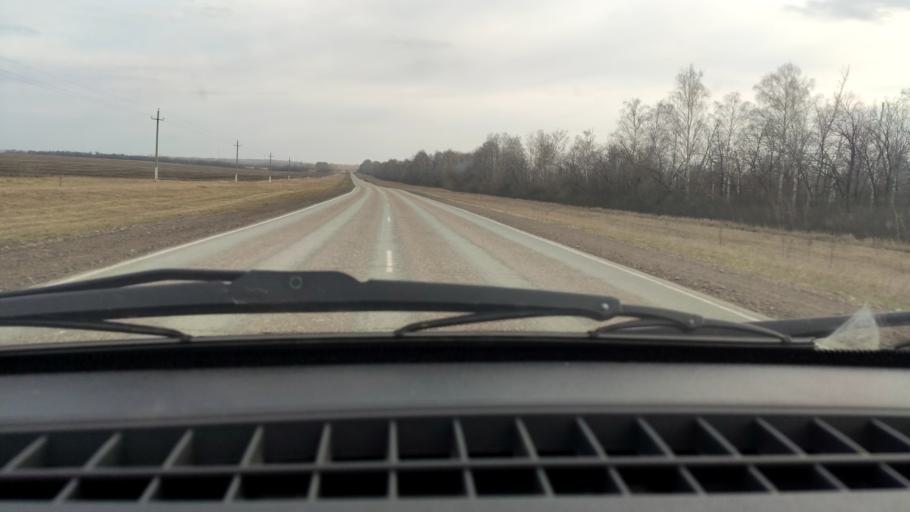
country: RU
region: Bashkortostan
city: Davlekanovo
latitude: 54.3294
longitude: 55.1656
